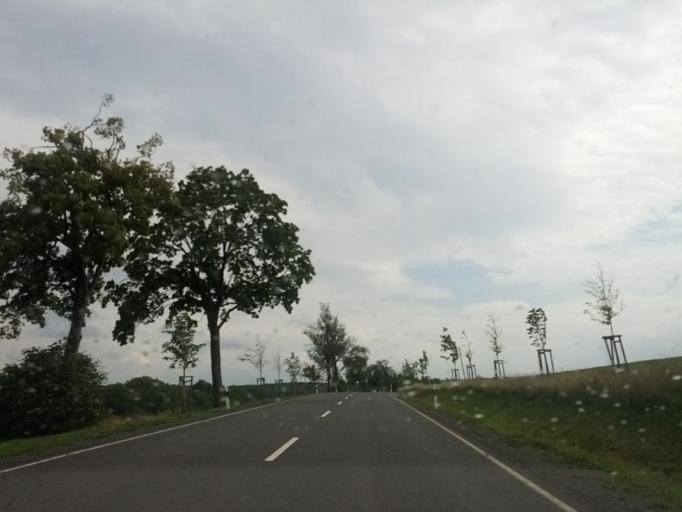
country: DE
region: Thuringia
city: Georgenthal
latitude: 50.8553
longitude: 10.6473
